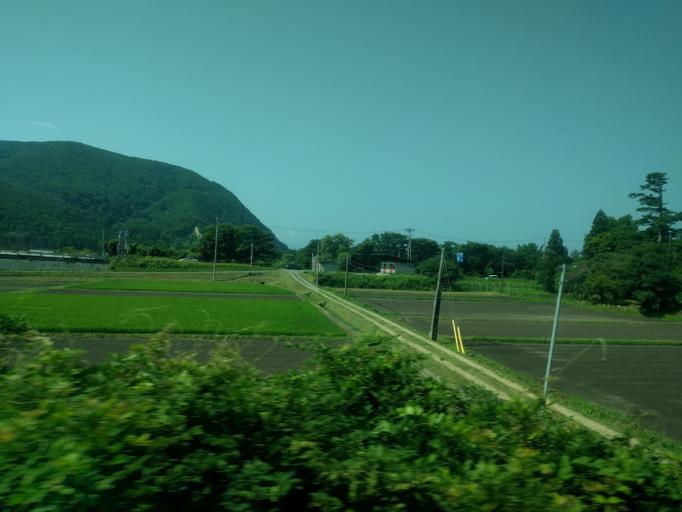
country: JP
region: Fukushima
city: Inawashiro
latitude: 37.4906
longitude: 140.1577
